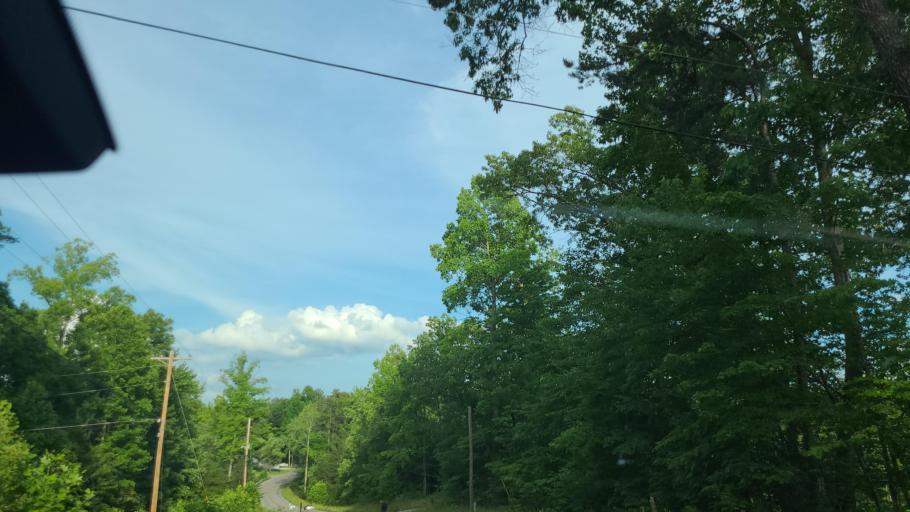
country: US
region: Kentucky
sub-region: Whitley County
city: Corbin
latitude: 36.9119
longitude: -84.2504
